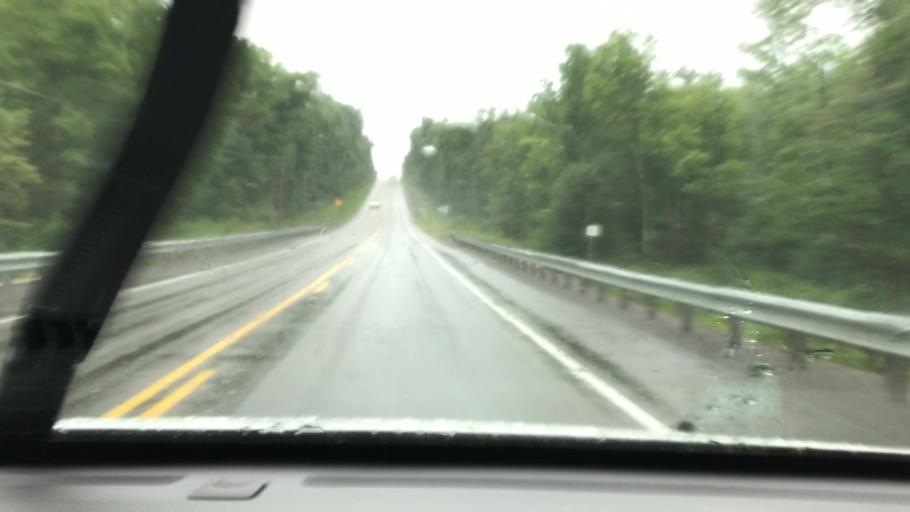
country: US
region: Pennsylvania
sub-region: Clearfield County
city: Osceola Mills
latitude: 40.8342
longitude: -78.2240
